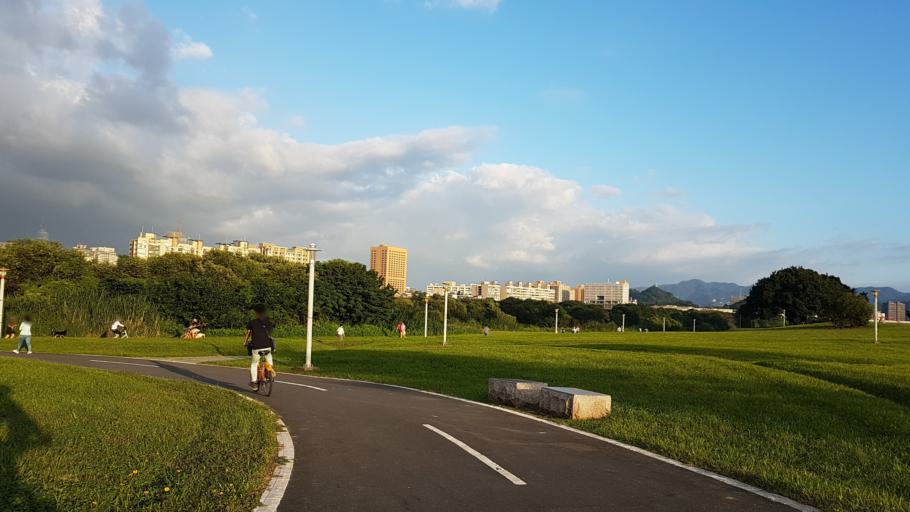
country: TW
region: Taipei
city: Taipei
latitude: 25.0185
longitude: 121.5180
